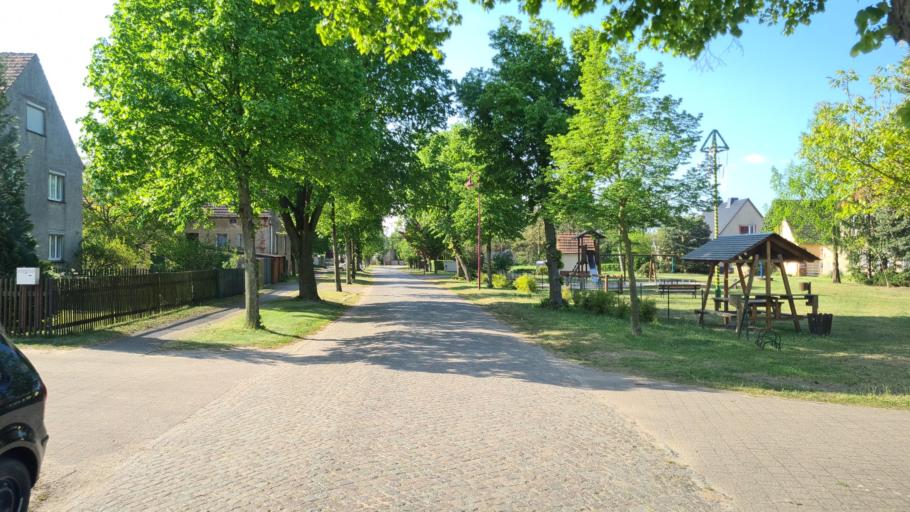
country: DE
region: Saxony
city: Arzberg
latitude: 51.5868
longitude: 13.1749
